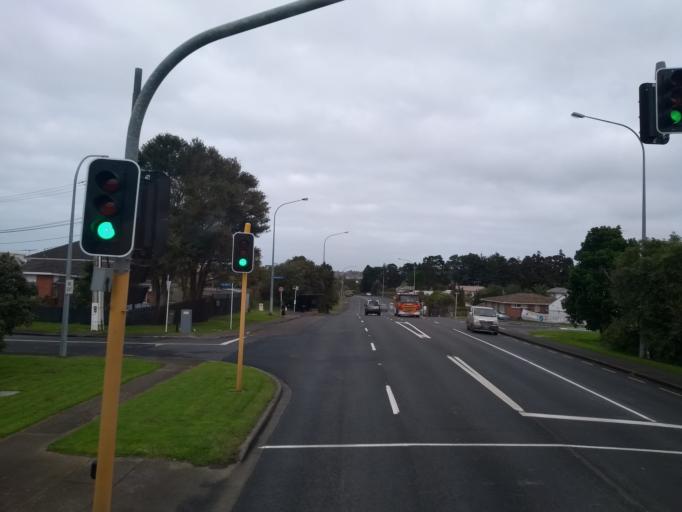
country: NZ
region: Auckland
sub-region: Auckland
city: Tamaki
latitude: -36.8983
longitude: 174.8231
